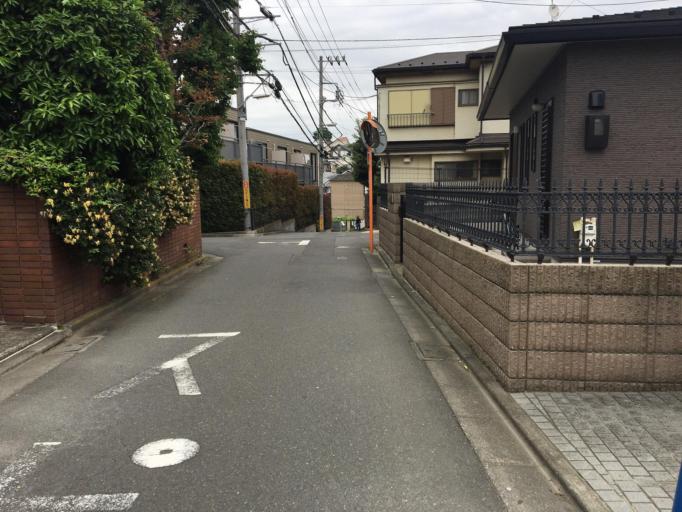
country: JP
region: Tokyo
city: Chofugaoka
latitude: 35.6577
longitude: 139.5790
